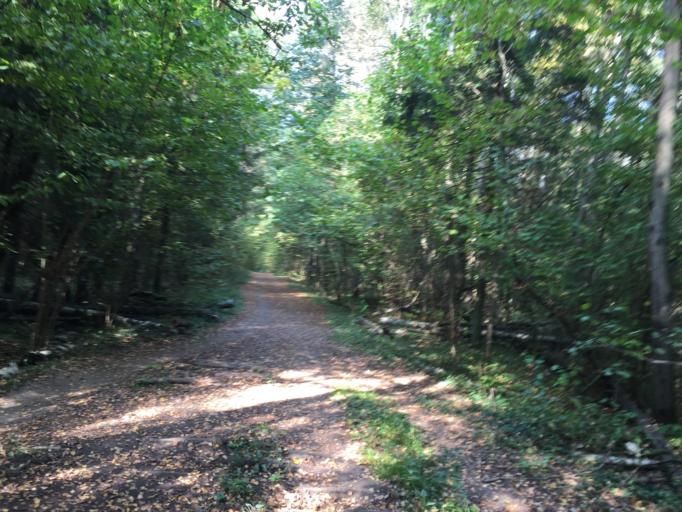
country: RU
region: Moscow
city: Babushkin
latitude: 55.8652
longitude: 37.7427
